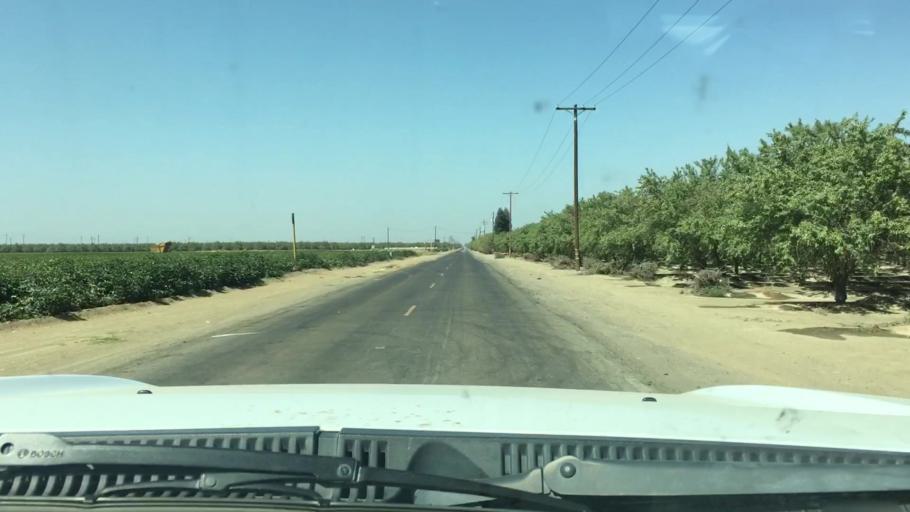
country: US
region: California
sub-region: Kern County
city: Shafter
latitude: 35.4798
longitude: -119.3141
